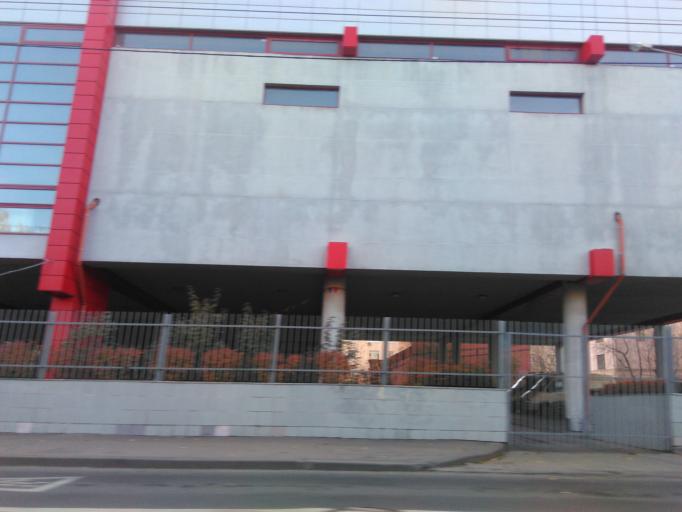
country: RU
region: Moscow
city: Mar'ina Roshcha
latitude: 55.7894
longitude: 37.6165
